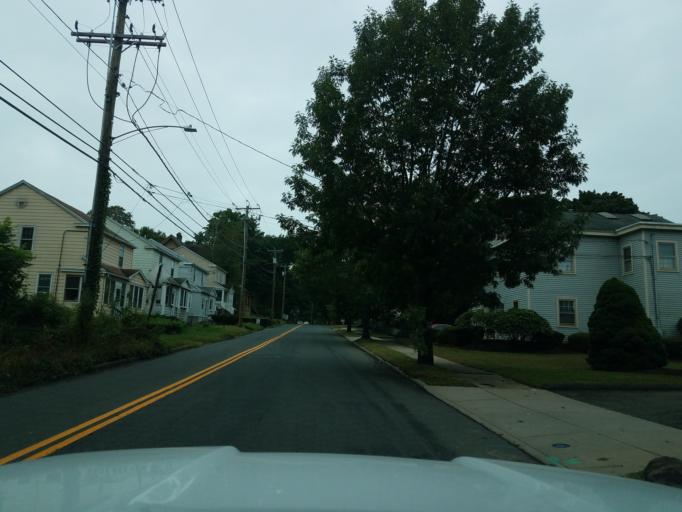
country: US
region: Connecticut
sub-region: New Haven County
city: East Haven
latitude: 41.3153
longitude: -72.8777
